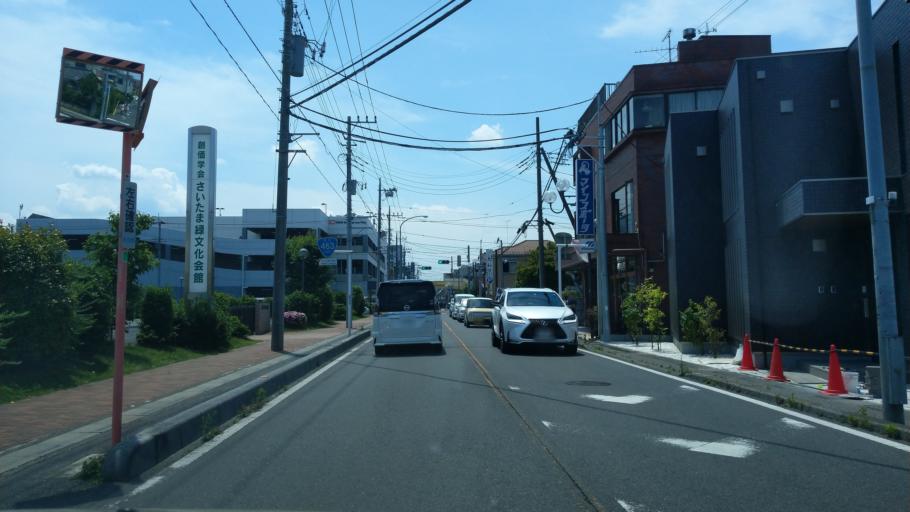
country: JP
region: Saitama
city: Saitama
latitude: 35.8712
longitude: 139.6737
